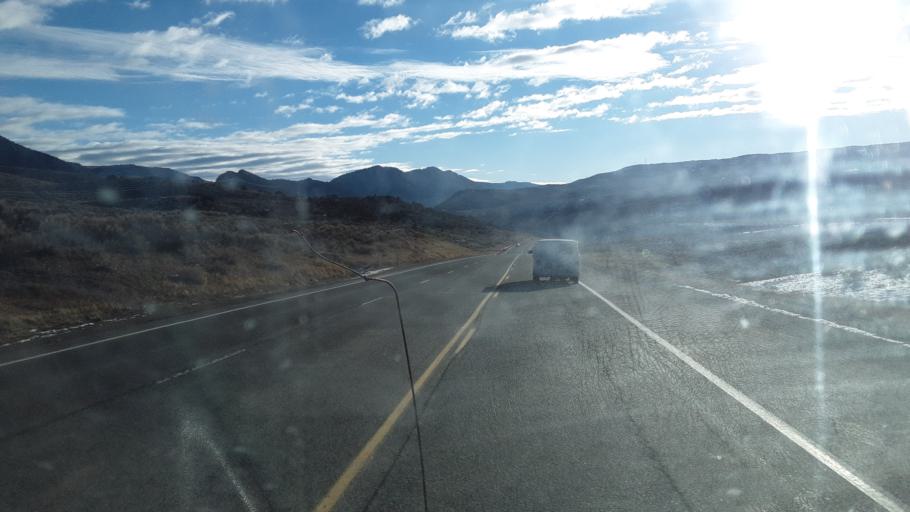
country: US
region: Colorado
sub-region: Montrose County
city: Montrose
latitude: 38.4425
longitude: -107.6079
